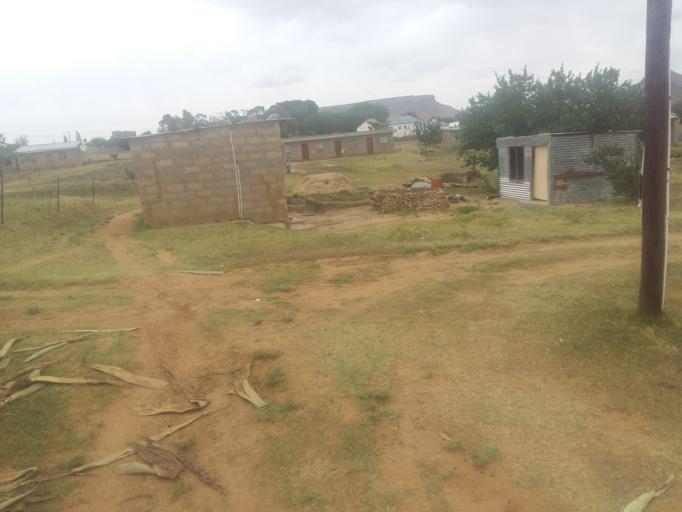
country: LS
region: Mafeteng
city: Mafeteng
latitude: -29.6993
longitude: 27.4352
